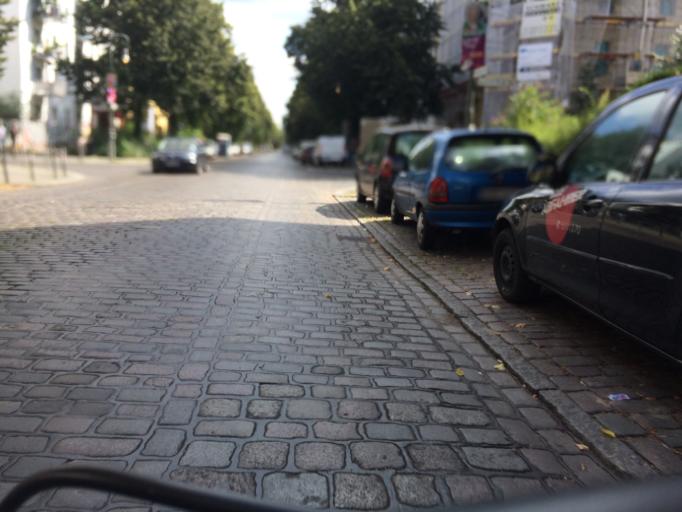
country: DE
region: Berlin
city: Berlin Treptow
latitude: 52.4965
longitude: 13.4272
